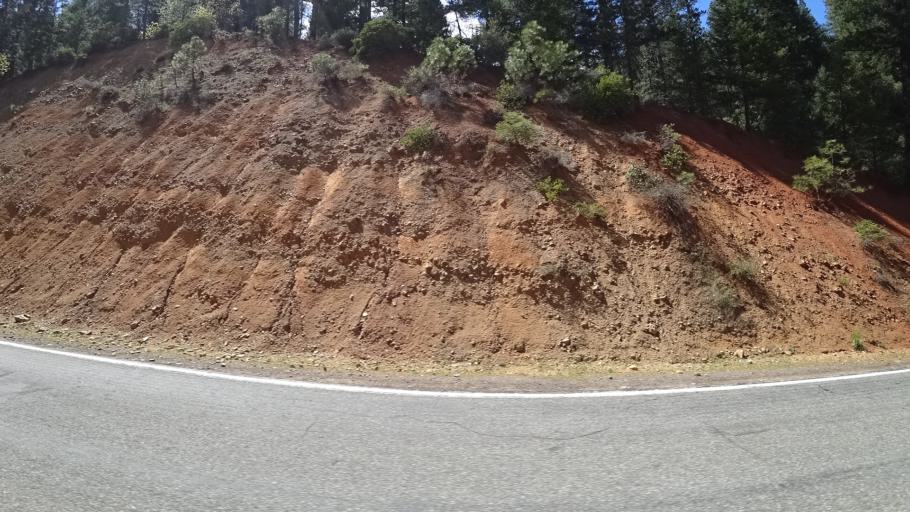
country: US
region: California
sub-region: Trinity County
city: Weaverville
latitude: 40.7927
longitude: -122.8938
